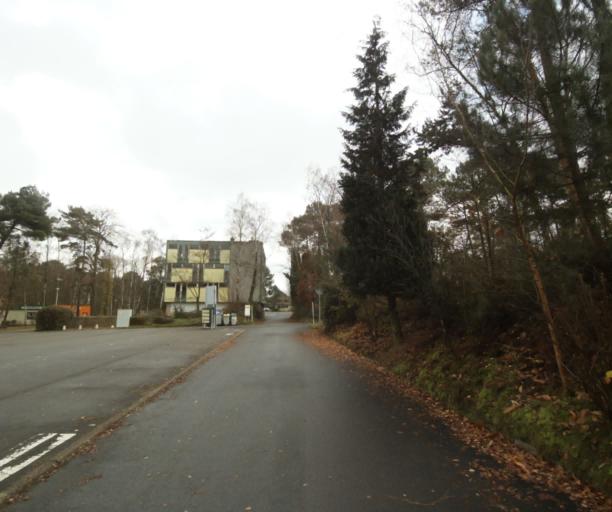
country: FR
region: Pays de la Loire
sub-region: Departement de la Sarthe
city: Le Mans
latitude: 47.9833
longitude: 0.2288
